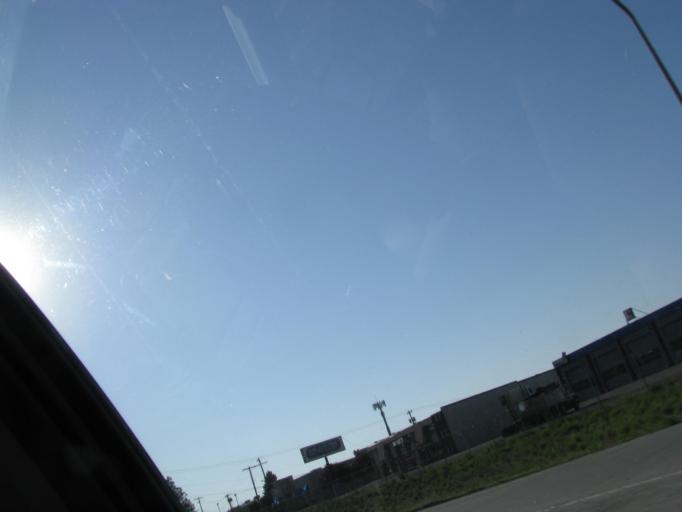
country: US
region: Washington
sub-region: Spokane County
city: Dishman
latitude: 47.6541
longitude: -117.3282
